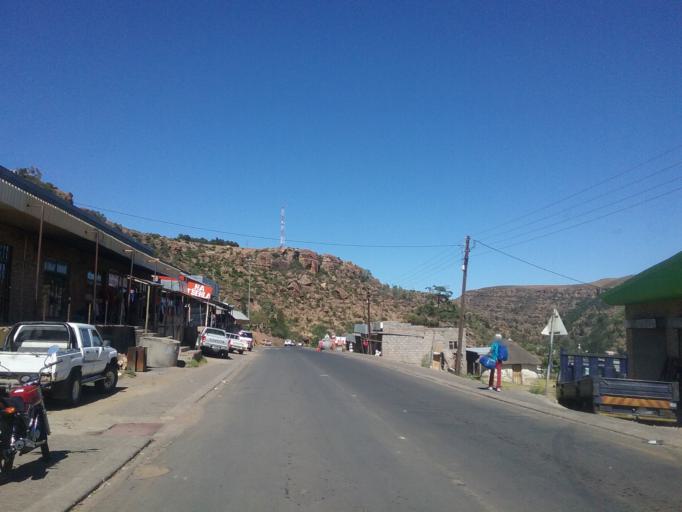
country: LS
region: Quthing
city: Quthing
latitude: -30.4001
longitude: 27.6997
